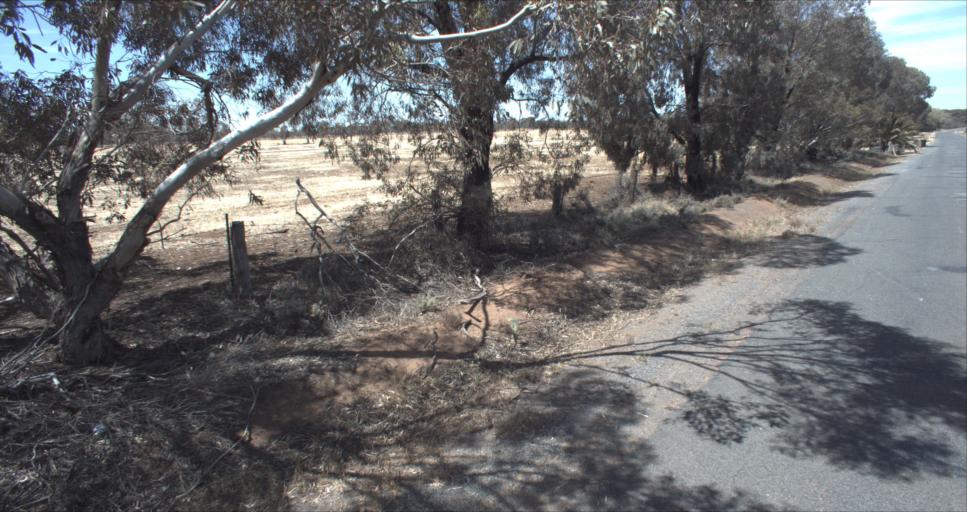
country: AU
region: New South Wales
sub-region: Leeton
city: Leeton
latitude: -34.5872
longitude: 146.4277
